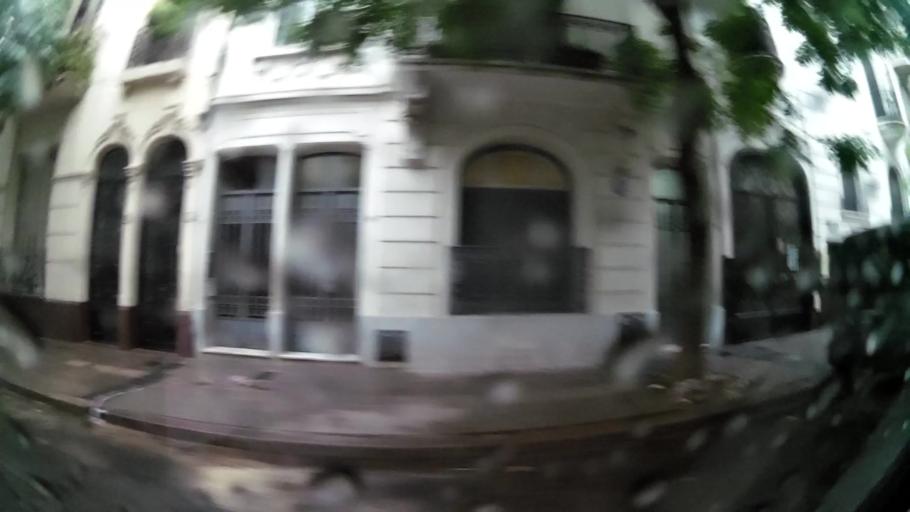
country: AR
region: Buenos Aires F.D.
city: Buenos Aires
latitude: -34.6307
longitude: -58.3764
